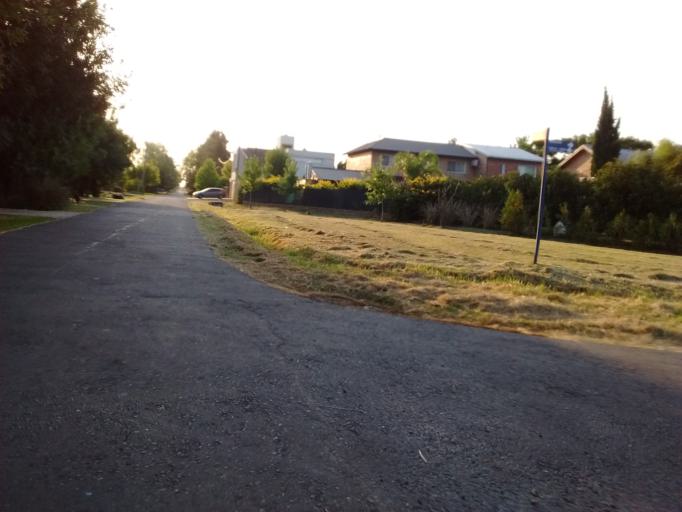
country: AR
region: Santa Fe
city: Funes
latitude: -32.9161
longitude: -60.7563
